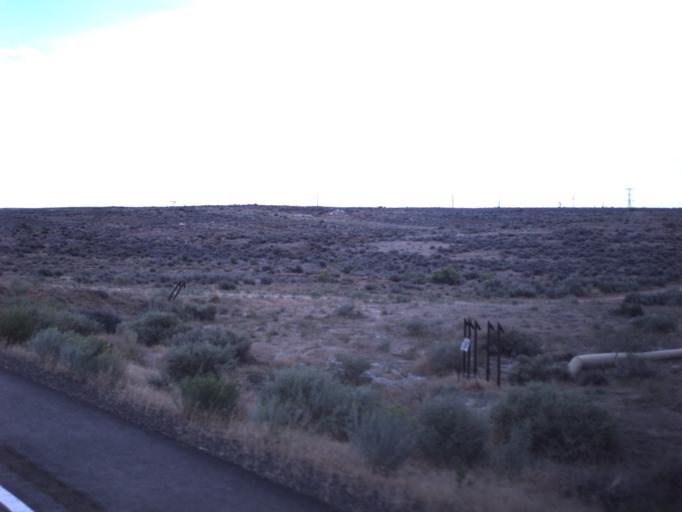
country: US
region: Utah
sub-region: Uintah County
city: Naples
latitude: 40.2103
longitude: -109.3705
